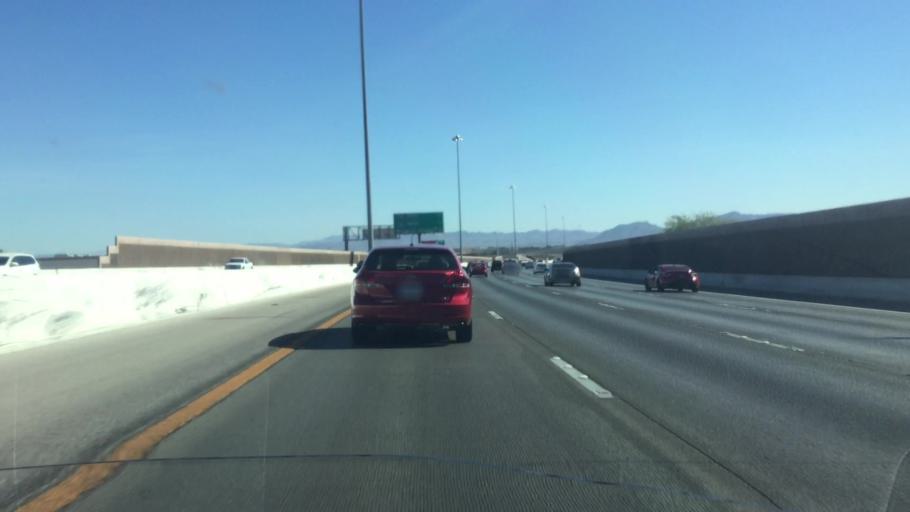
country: US
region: Nevada
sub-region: Clark County
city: Paradise
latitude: 36.0685
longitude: -115.1982
